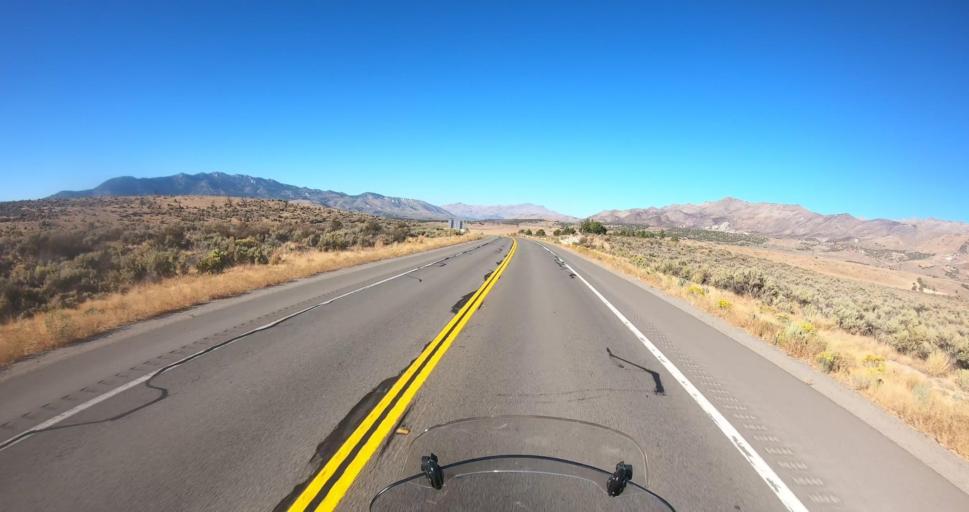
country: US
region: Nevada
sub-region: Washoe County
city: Cold Springs
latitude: 39.8048
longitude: -120.0349
